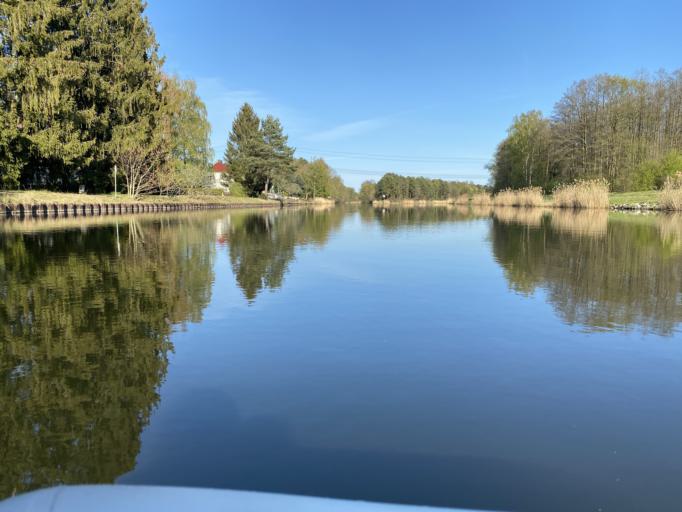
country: DE
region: Brandenburg
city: Mullrose
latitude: 52.2468
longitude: 14.4569
